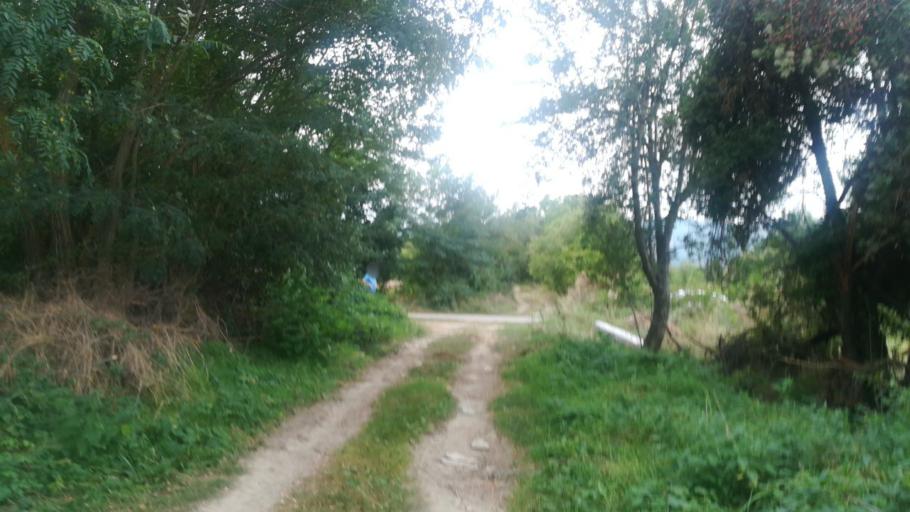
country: MK
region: Debarca
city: Belcista
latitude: 41.2853
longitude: 20.8305
